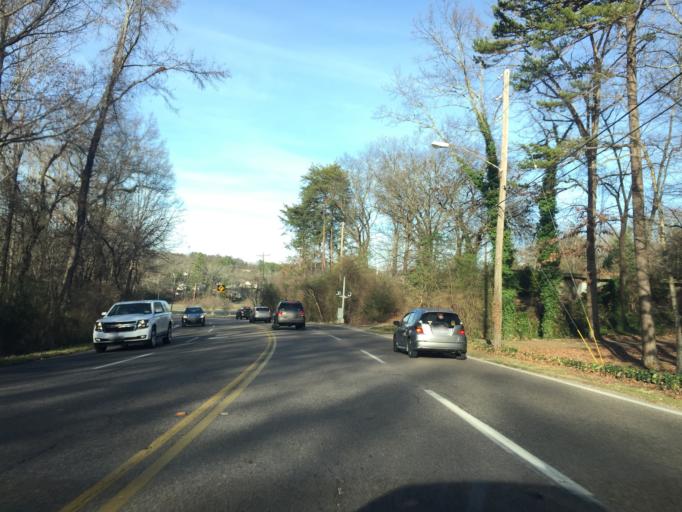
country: US
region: Tennessee
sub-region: Hamilton County
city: Red Bank
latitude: 35.0971
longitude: -85.2813
